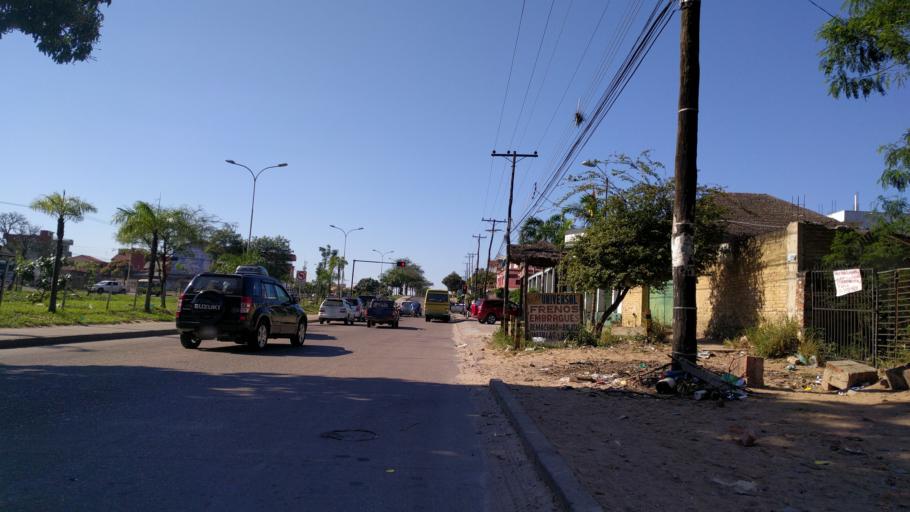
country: BO
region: Santa Cruz
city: Santa Cruz de la Sierra
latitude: -17.8165
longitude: -63.2031
